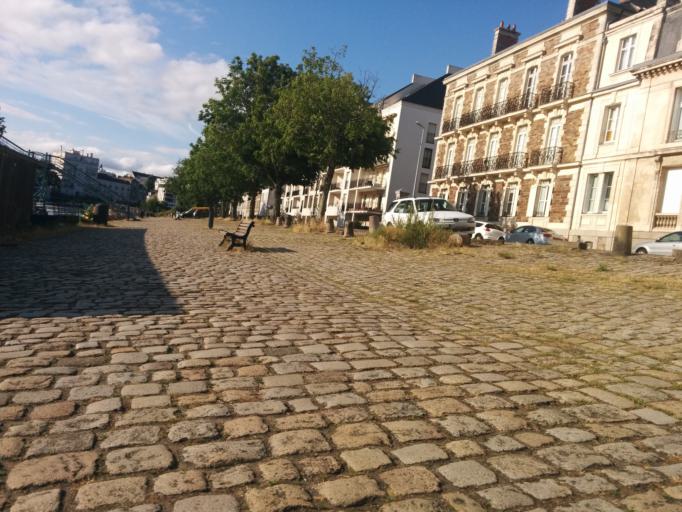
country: FR
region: Pays de la Loire
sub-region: Departement de la Loire-Atlantique
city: Nantes
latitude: 47.2248
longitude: -1.5530
